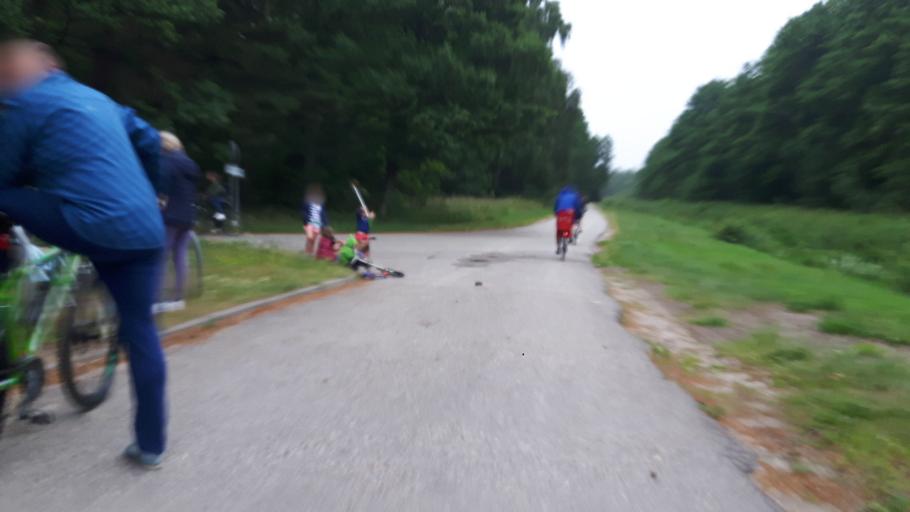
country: LT
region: Klaipedos apskritis
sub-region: Palanga
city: Sventoji
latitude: 55.9787
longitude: 21.0741
